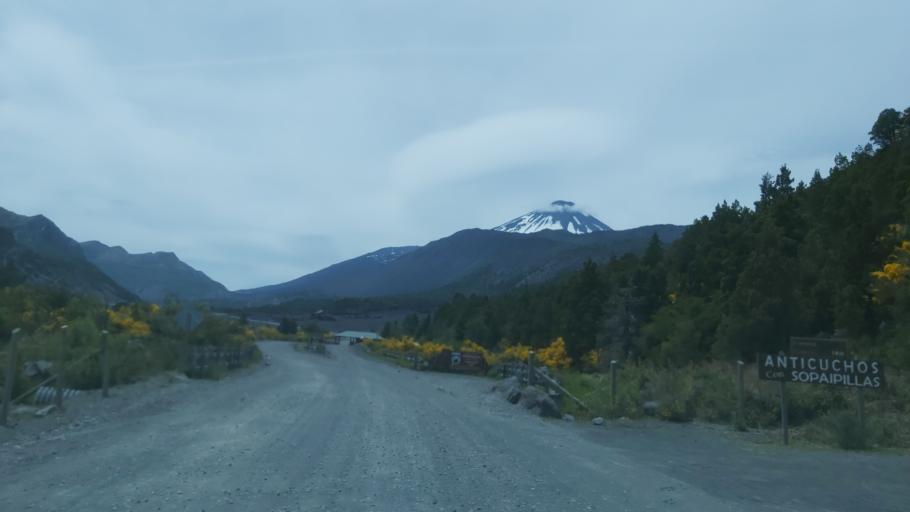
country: AR
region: Neuquen
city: Andacollo
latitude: -37.3986
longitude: -71.4427
